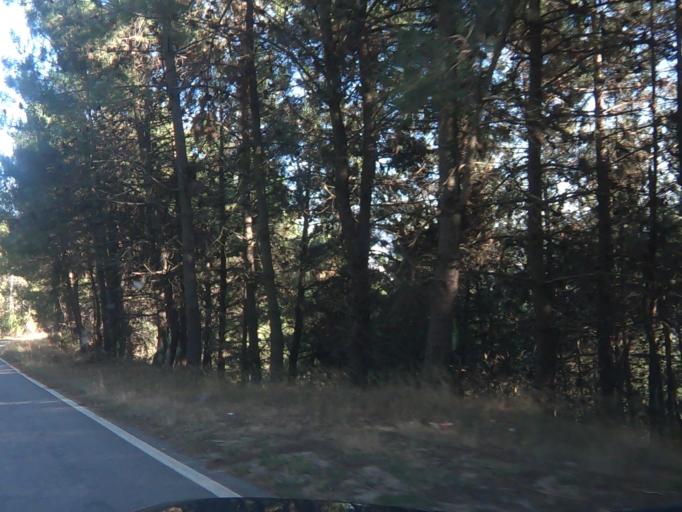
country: PT
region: Vila Real
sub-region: Vila Real
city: Vila Real
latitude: 41.3352
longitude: -7.7755
